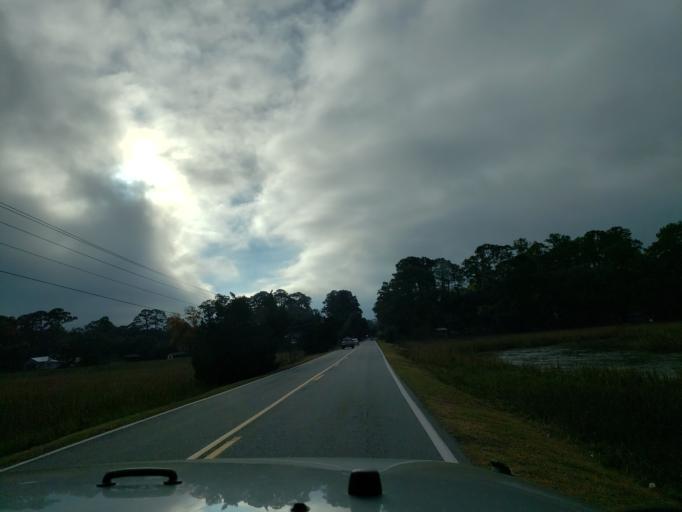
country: US
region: Georgia
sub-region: Chatham County
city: Wilmington Island
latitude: 32.0177
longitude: -80.9620
